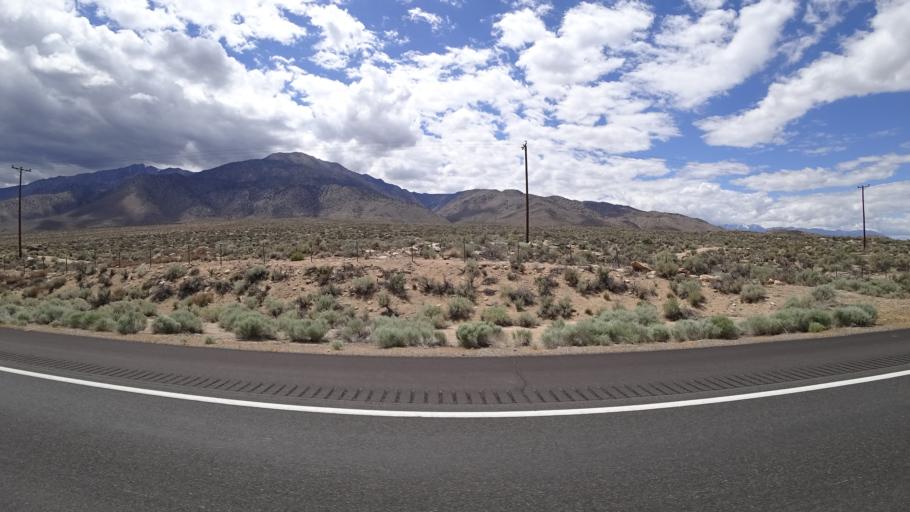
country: US
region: California
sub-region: Inyo County
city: Bishop
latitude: 37.2933
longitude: -118.3749
